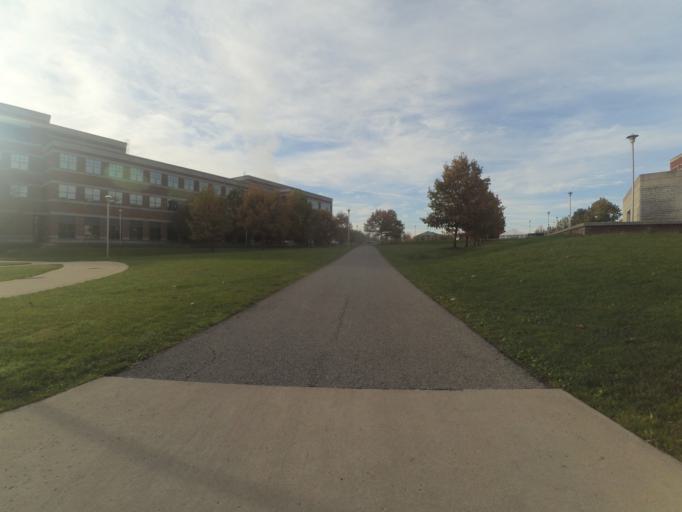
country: US
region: Pennsylvania
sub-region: Centre County
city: State College
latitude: 40.7922
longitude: -77.8700
